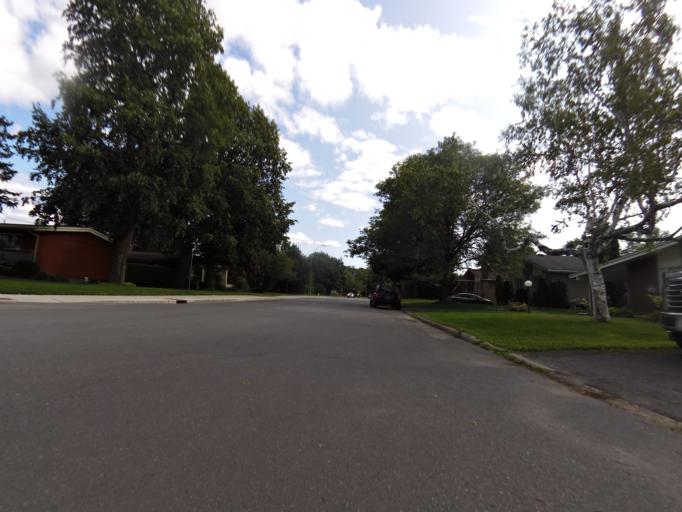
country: CA
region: Ontario
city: Ottawa
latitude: 45.3919
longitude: -75.6264
